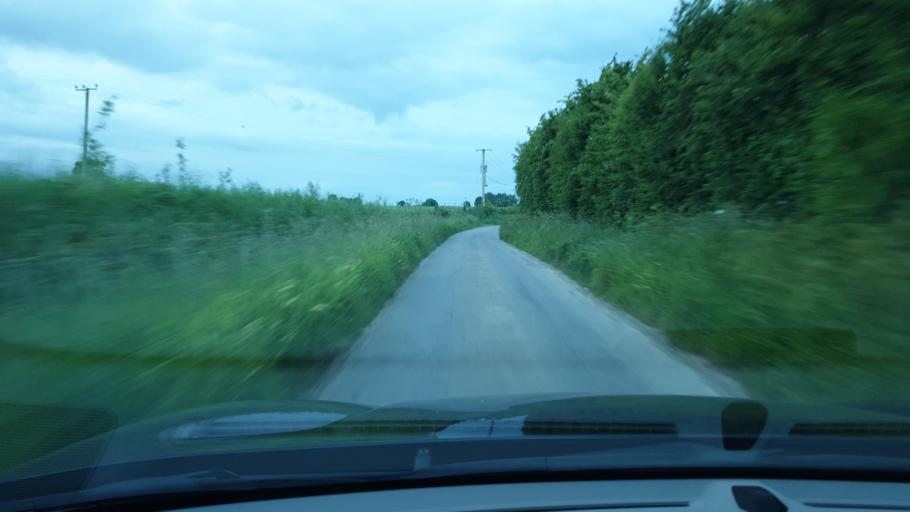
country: IE
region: Leinster
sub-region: An Mhi
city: Ashbourne
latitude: 53.5428
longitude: -6.3478
